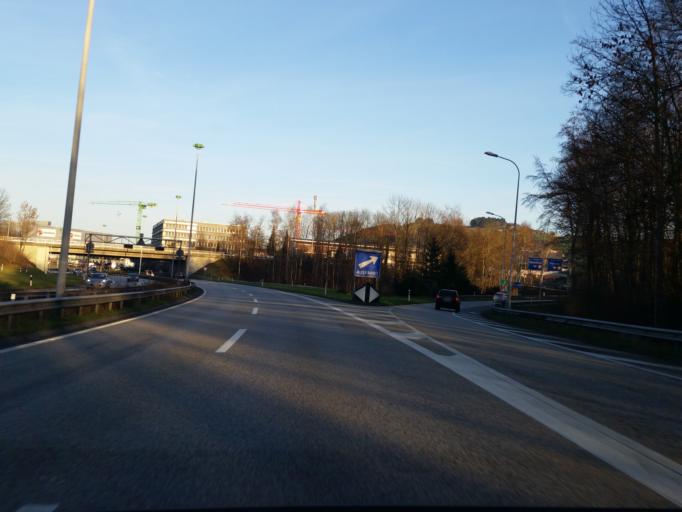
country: CH
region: Saint Gallen
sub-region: Wahlkreis Rorschach
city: Morschwil
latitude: 47.4391
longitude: 9.4133
